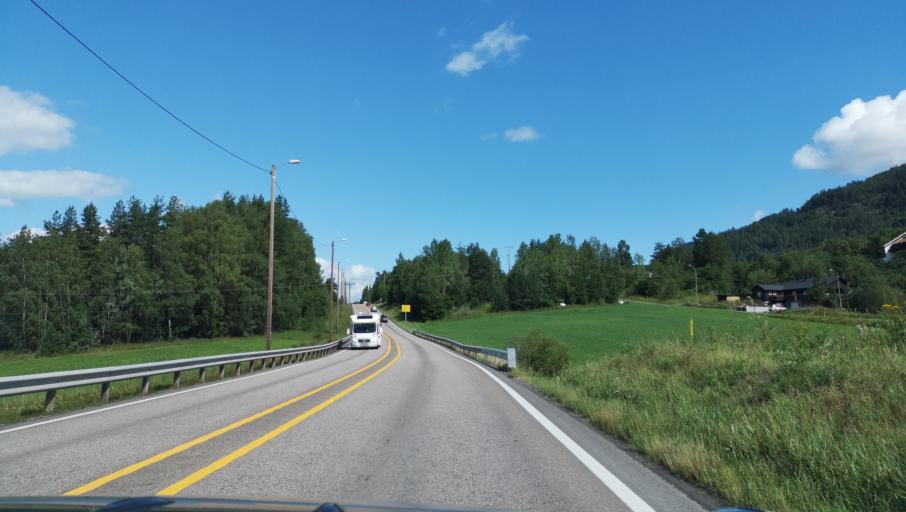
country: NO
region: Buskerud
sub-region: Ovre Eiker
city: Hokksund
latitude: 59.8483
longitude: 9.9172
